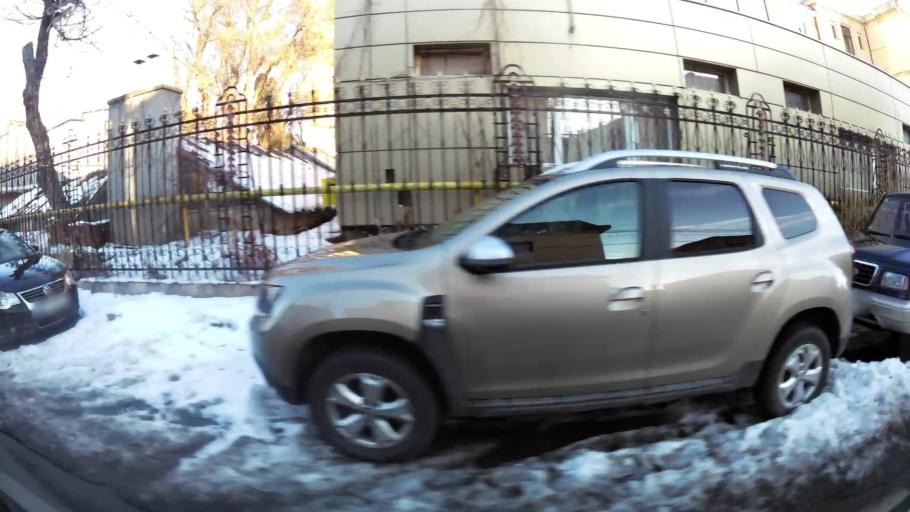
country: RO
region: Bucuresti
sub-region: Municipiul Bucuresti
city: Bucuresti
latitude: 44.4351
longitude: 26.0688
